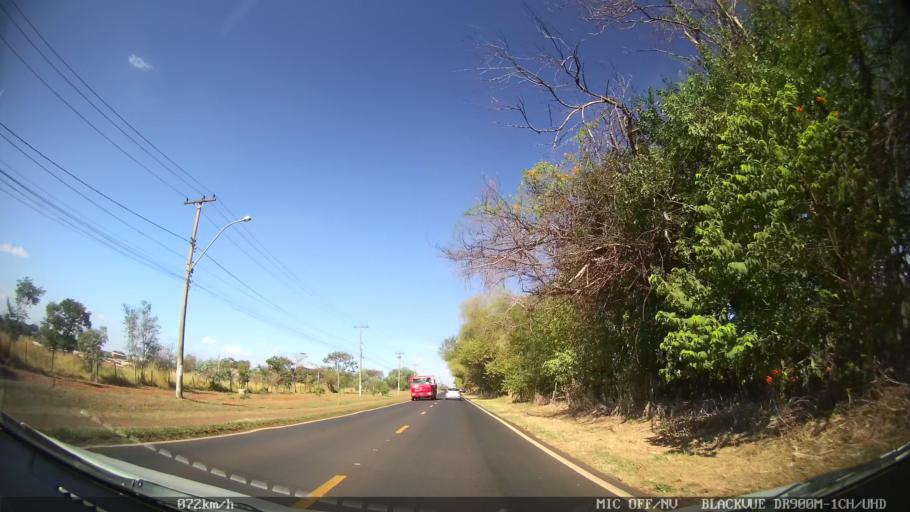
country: BR
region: Sao Paulo
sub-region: Ribeirao Preto
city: Ribeirao Preto
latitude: -21.1563
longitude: -47.7747
